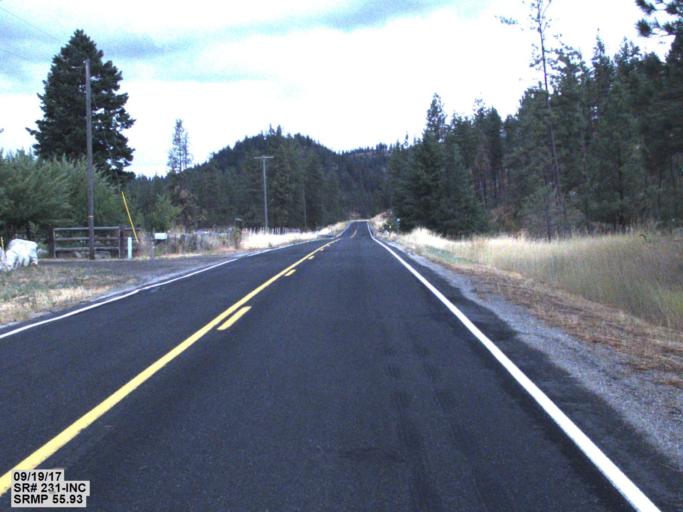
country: US
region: Washington
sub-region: Spokane County
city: Deer Park
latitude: 47.9717
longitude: -117.7375
